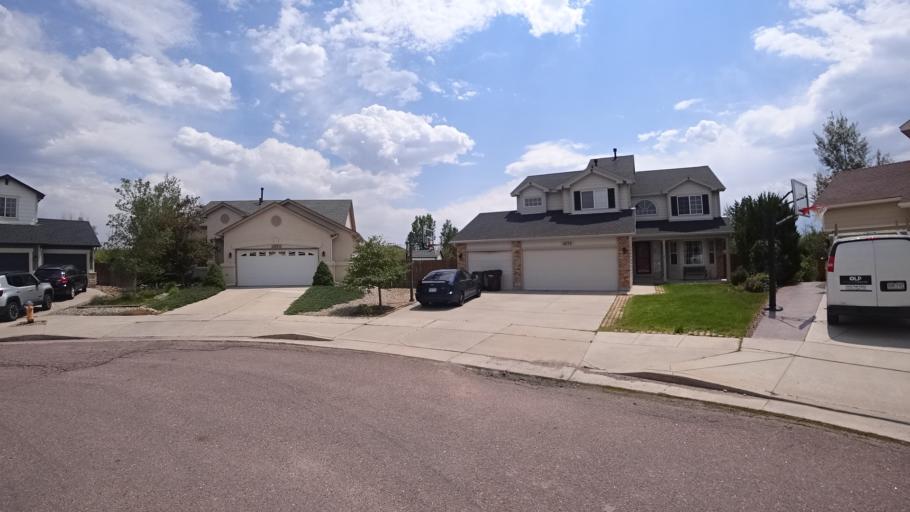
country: US
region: Colorado
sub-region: El Paso County
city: Black Forest
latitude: 38.9633
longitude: -104.7398
